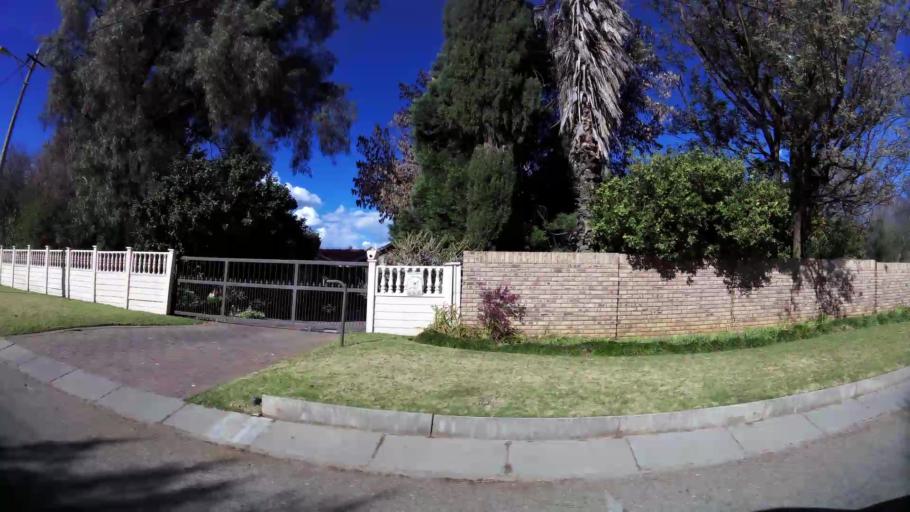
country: ZA
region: North-West
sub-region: Dr Kenneth Kaunda District Municipality
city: Klerksdorp
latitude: -26.8265
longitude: 26.6645
